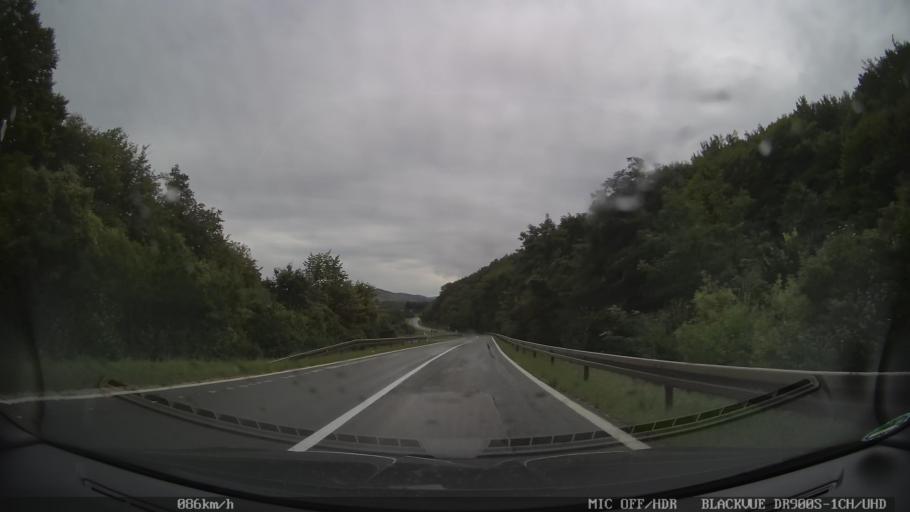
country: HR
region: Licko-Senjska
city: Brinje
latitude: 44.9599
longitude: 15.0927
